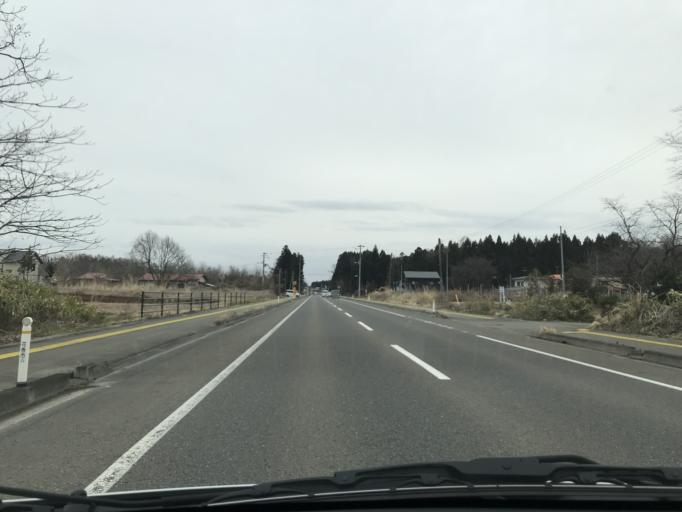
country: JP
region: Iwate
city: Hanamaki
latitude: 39.3658
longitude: 141.1112
